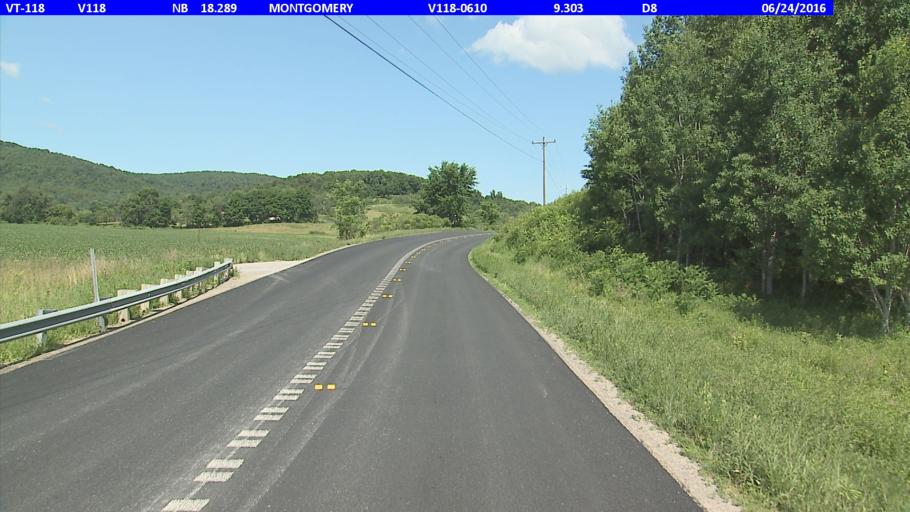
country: US
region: Vermont
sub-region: Franklin County
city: Richford
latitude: 44.9099
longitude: -72.6572
